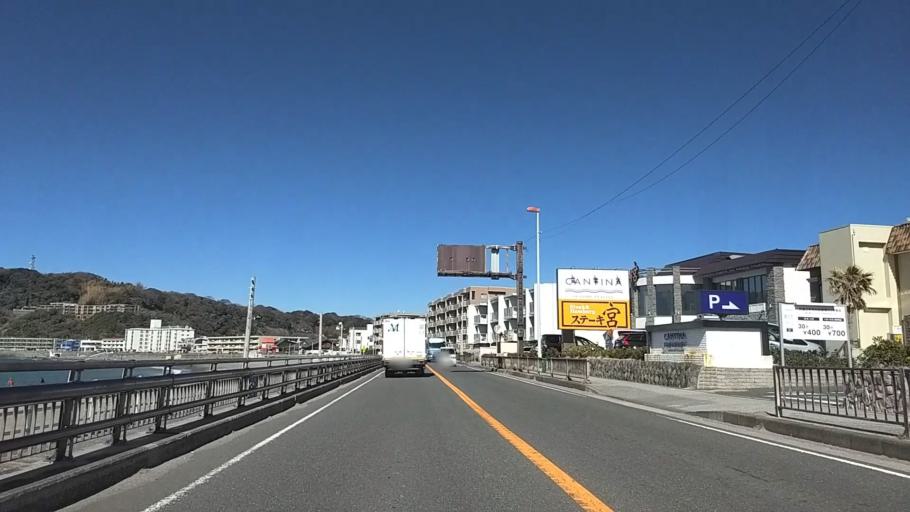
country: JP
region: Kanagawa
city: Zushi
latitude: 35.2908
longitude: 139.5736
